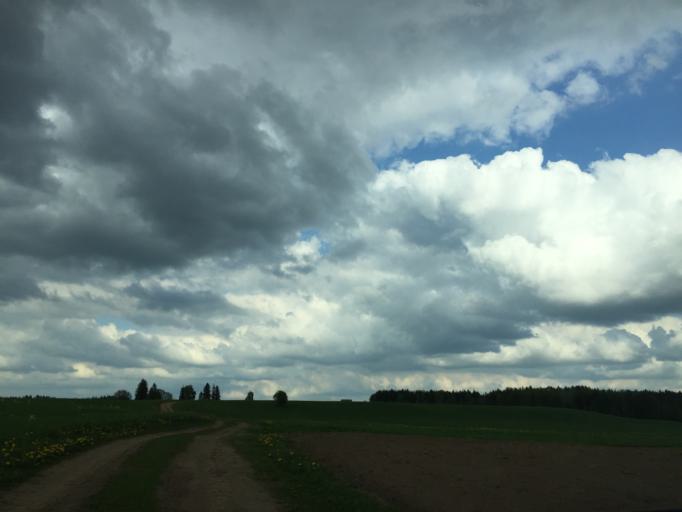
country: LV
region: Limbazu Rajons
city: Limbazi
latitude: 57.3703
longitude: 24.7668
